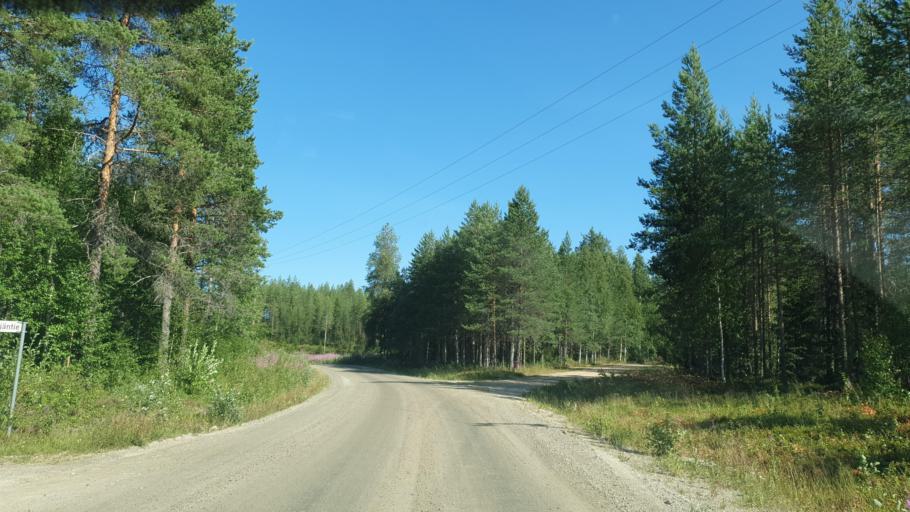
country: FI
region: Kainuu
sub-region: Kehys-Kainuu
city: Kuhmo
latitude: 64.0497
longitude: 29.6085
